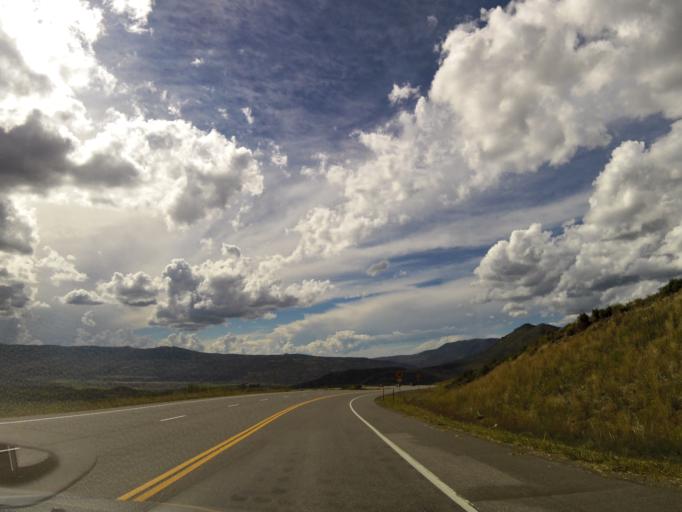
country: US
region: Colorado
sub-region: Hinsdale County
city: Lake City
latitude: 38.3959
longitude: -107.4491
